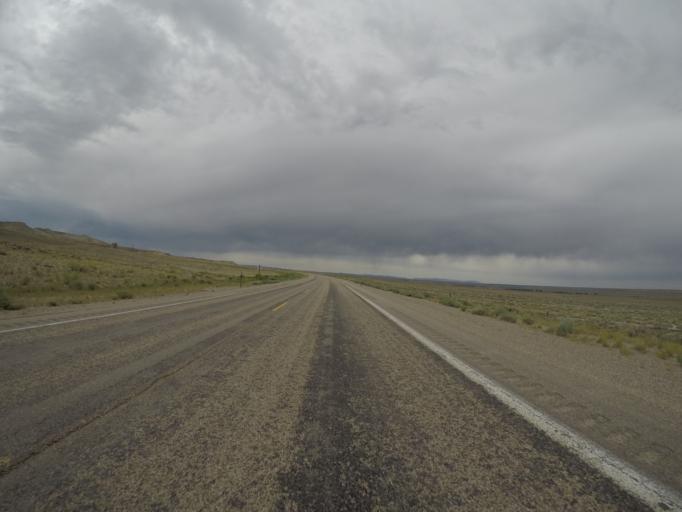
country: US
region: Wyoming
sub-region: Lincoln County
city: Kemmerer
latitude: 41.9493
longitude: -110.0154
